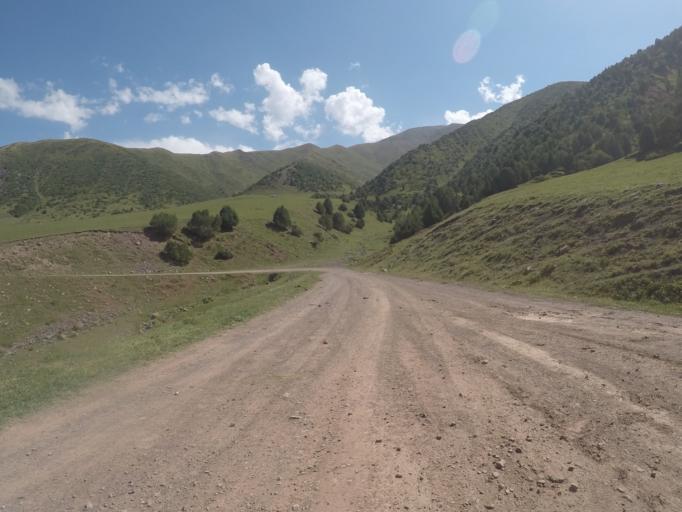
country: KG
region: Chuy
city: Bishkek
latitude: 42.6437
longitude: 74.5707
